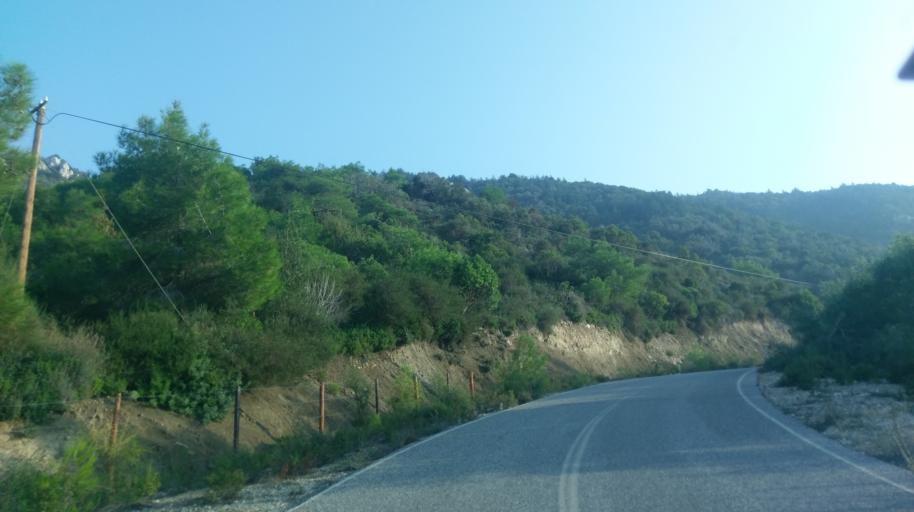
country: CY
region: Ammochostos
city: Trikomo
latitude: 35.4038
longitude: 33.9040
